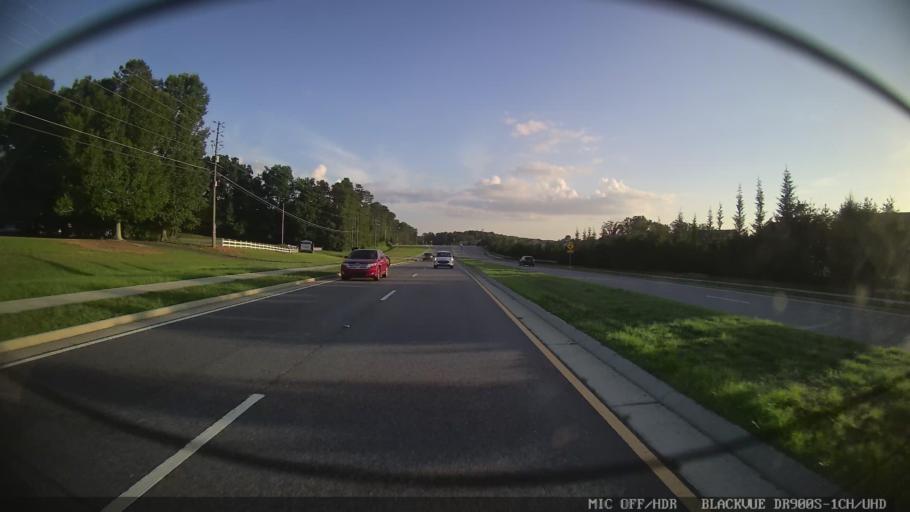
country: US
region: Georgia
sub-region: Forsyth County
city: Cumming
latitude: 34.2235
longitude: -84.1952
